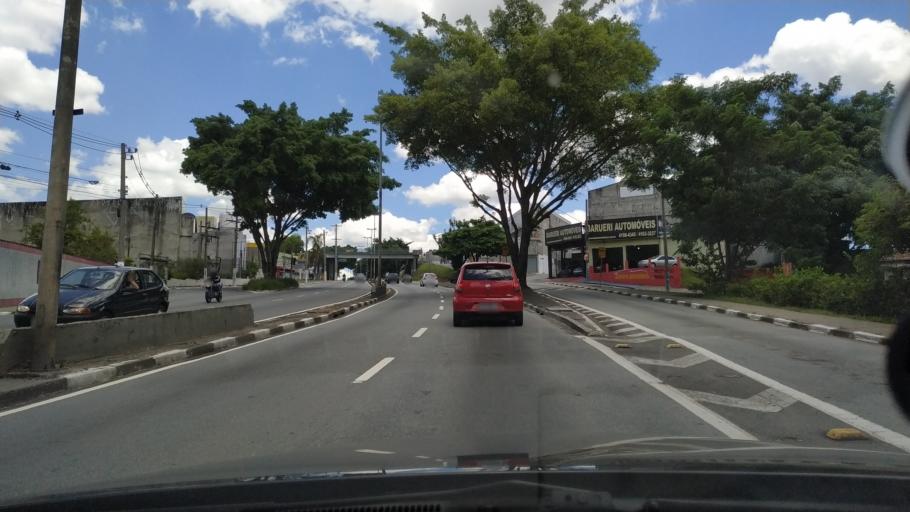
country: BR
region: Sao Paulo
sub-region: Barueri
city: Barueri
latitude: -23.4996
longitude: -46.8778
